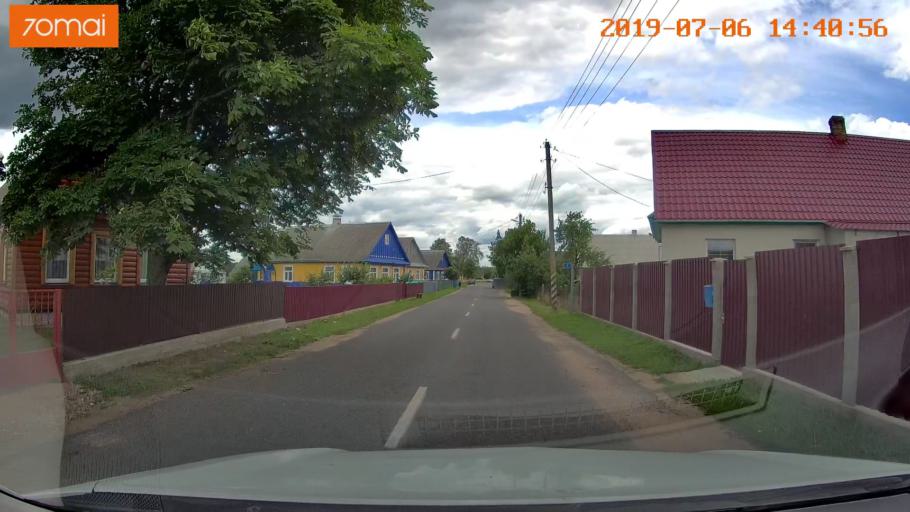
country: BY
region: Minsk
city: Ivyanyets
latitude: 53.9278
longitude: 26.6741
